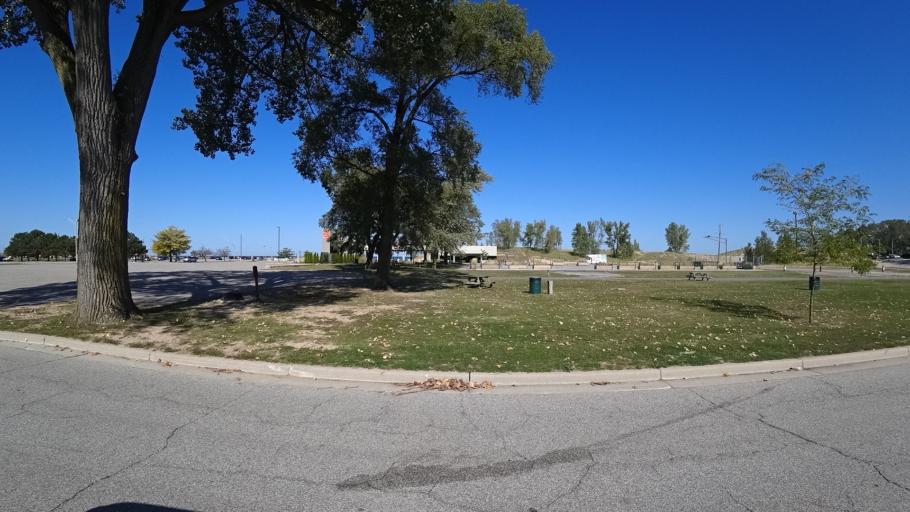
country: US
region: Indiana
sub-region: LaPorte County
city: Michigan City
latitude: 41.7260
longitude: -86.9024
